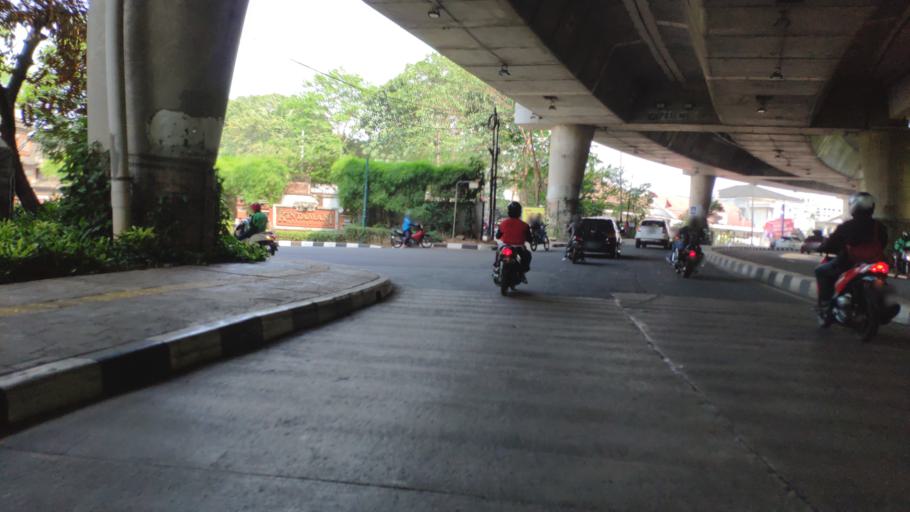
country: ID
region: Jakarta Raya
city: Jakarta
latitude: -6.2496
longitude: 106.8089
